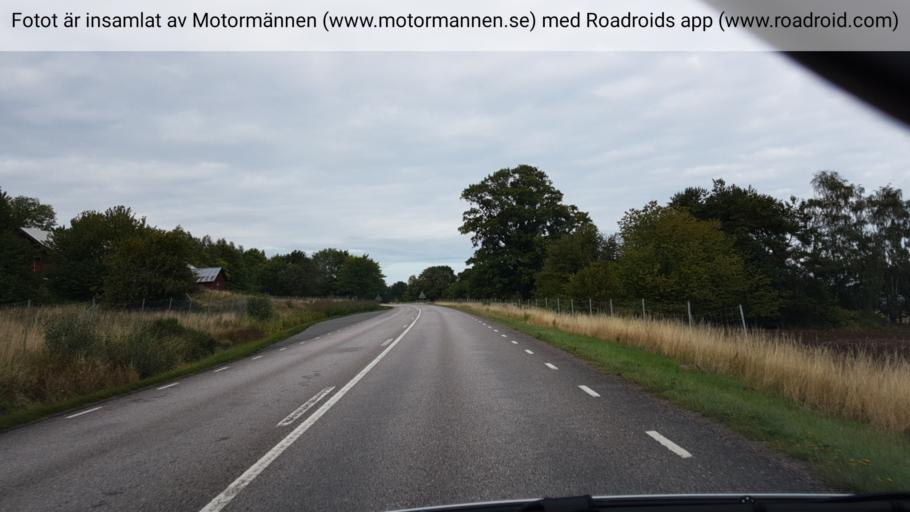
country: SE
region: Vaestra Goetaland
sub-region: Hjo Kommun
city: Hjo
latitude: 58.3311
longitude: 14.3327
